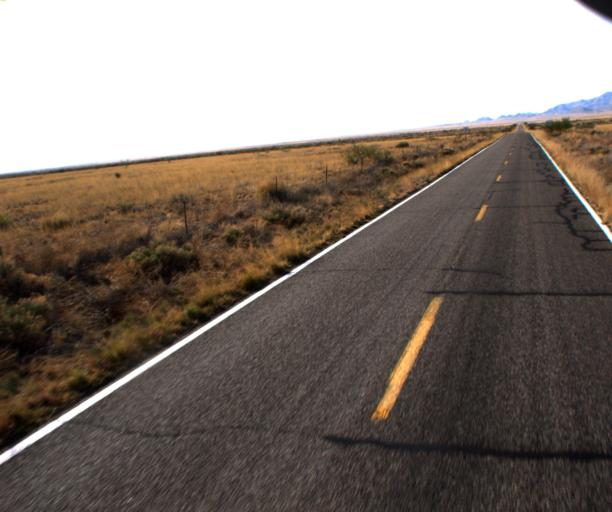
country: US
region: Arizona
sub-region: Cochise County
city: Willcox
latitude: 32.0441
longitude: -109.4851
